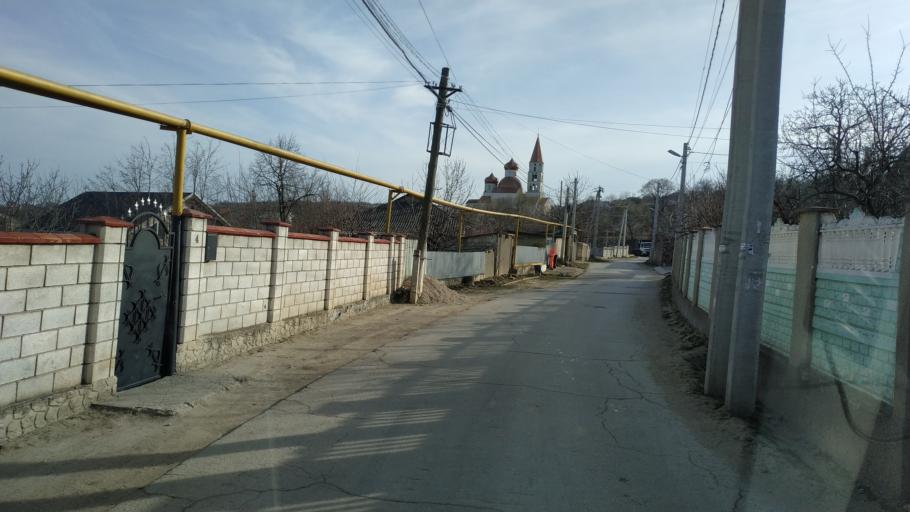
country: MD
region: Chisinau
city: Vatra
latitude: 47.0688
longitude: 28.6744
